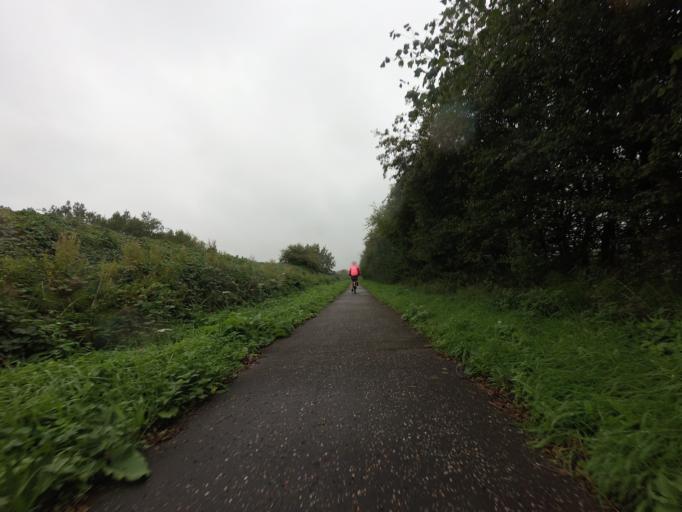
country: GB
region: England
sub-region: Norfolk
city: Dersingham
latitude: 52.8070
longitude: 0.4849
